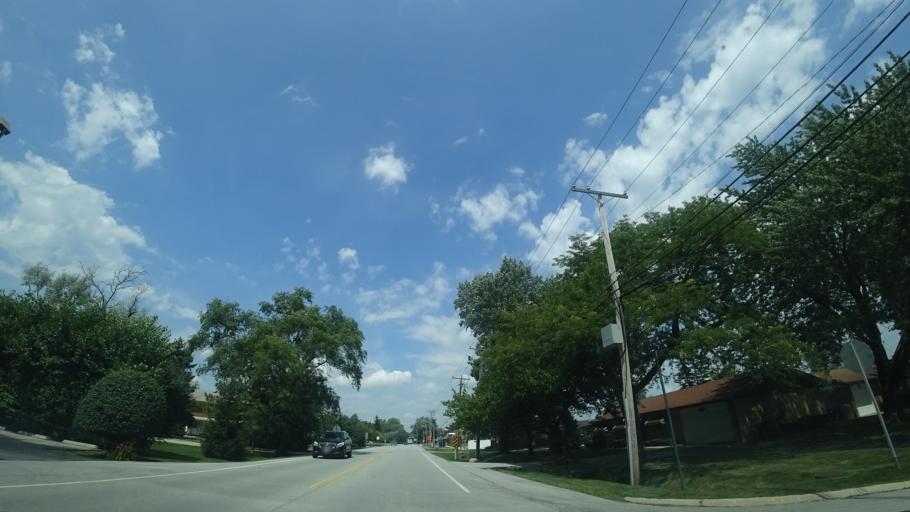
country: US
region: Illinois
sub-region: Cook County
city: Crestwood
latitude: 41.6592
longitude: -87.7580
